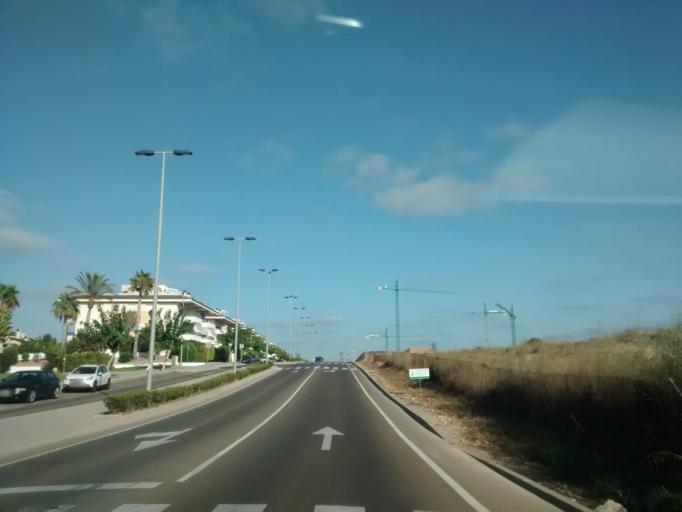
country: ES
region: Valencia
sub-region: Provincia de Alicante
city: Pilar de la Horadada
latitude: 37.8823
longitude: -0.7620
